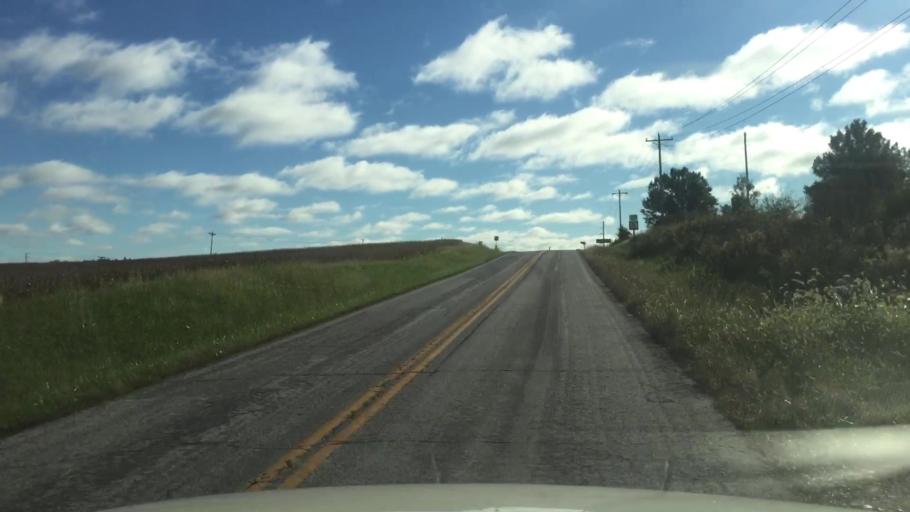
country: US
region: Missouri
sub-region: Howard County
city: Fayette
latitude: 39.1044
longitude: -92.7365
